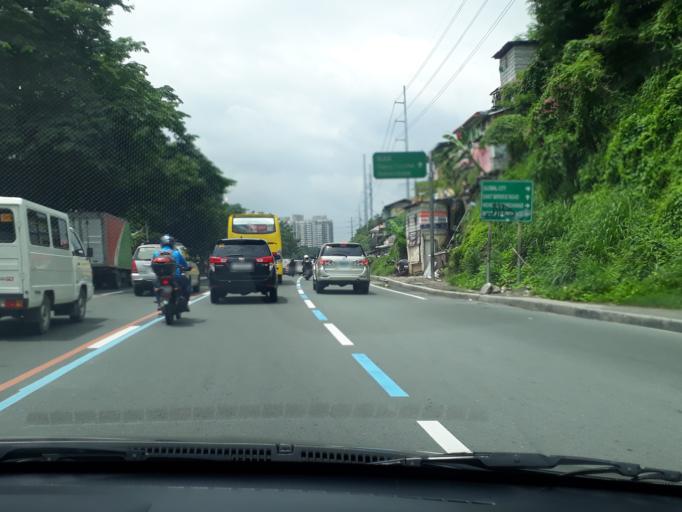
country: PH
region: Calabarzon
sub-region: Province of Rizal
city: Pateros
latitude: 14.5385
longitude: 121.0573
